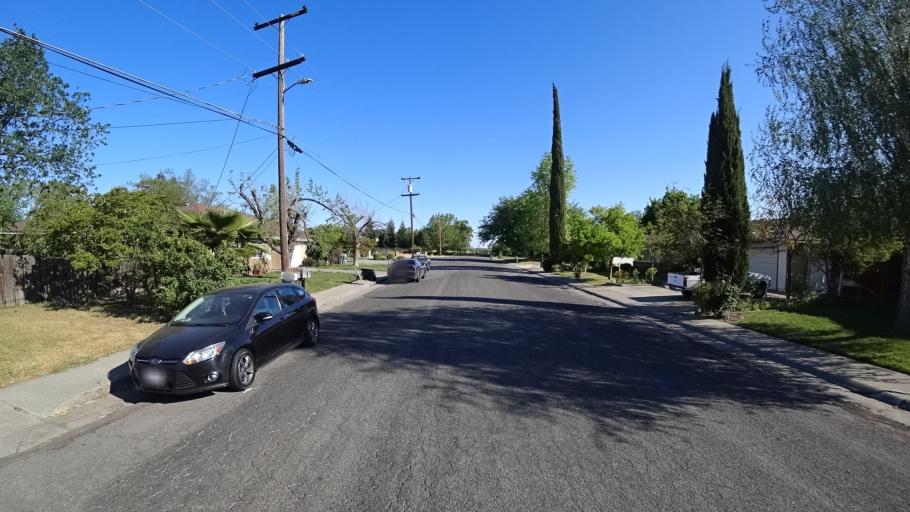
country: US
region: California
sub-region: Glenn County
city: Orland
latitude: 39.7517
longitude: -122.1835
